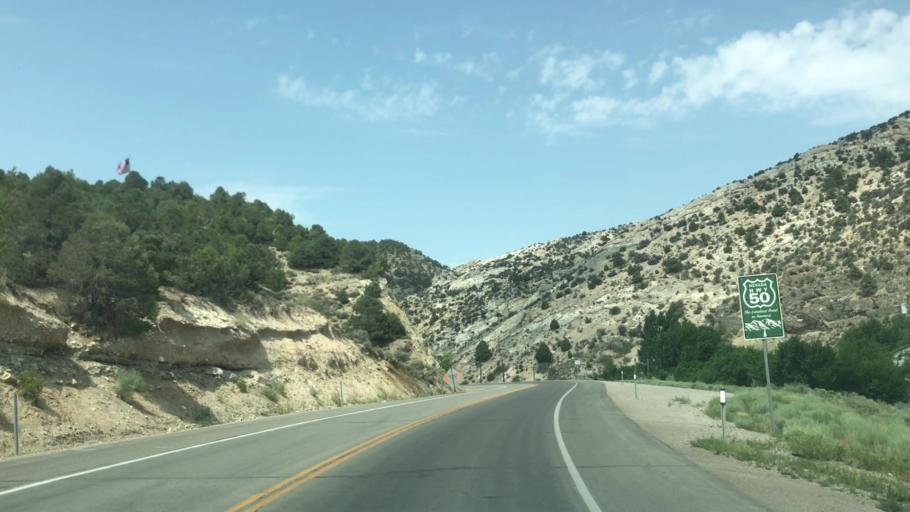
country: US
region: Nevada
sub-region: White Pine County
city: Ely
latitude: 39.2473
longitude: -114.8987
